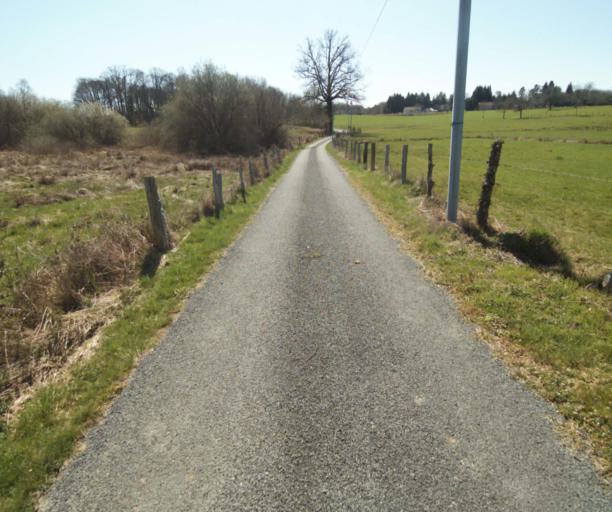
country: FR
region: Limousin
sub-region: Departement de la Correze
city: Saint-Mexant
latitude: 45.2763
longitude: 1.6757
